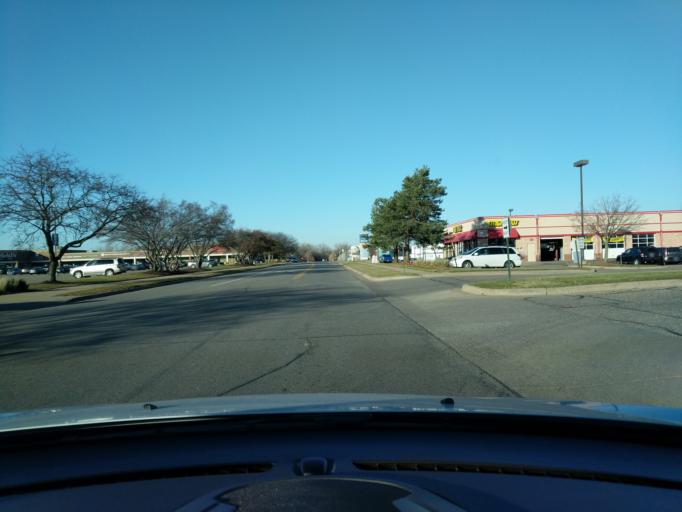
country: US
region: Minnesota
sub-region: Ramsey County
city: Roseville
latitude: 45.0227
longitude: -93.1690
